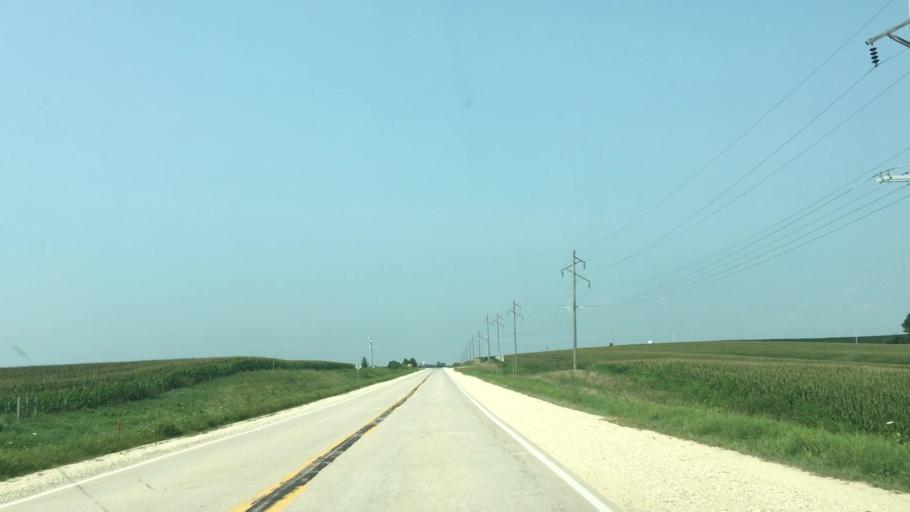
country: US
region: Iowa
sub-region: Winneshiek County
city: Decorah
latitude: 43.1443
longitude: -91.8642
